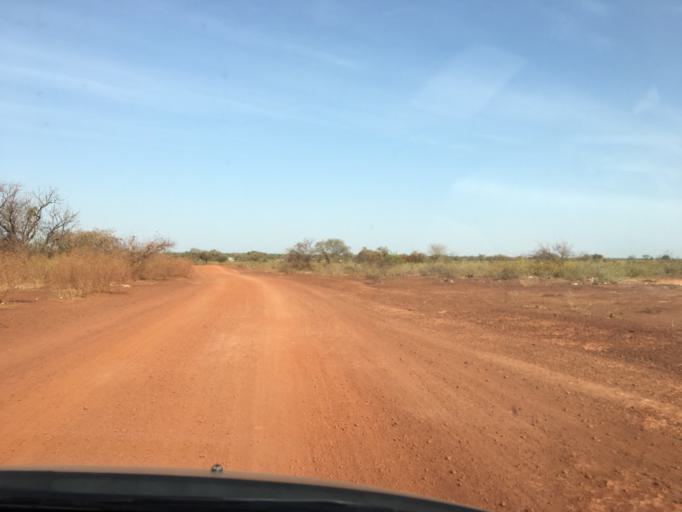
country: BF
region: Plateau-Central
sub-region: Province du Kourweogo
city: Bousse
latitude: 12.5623
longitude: -1.9029
